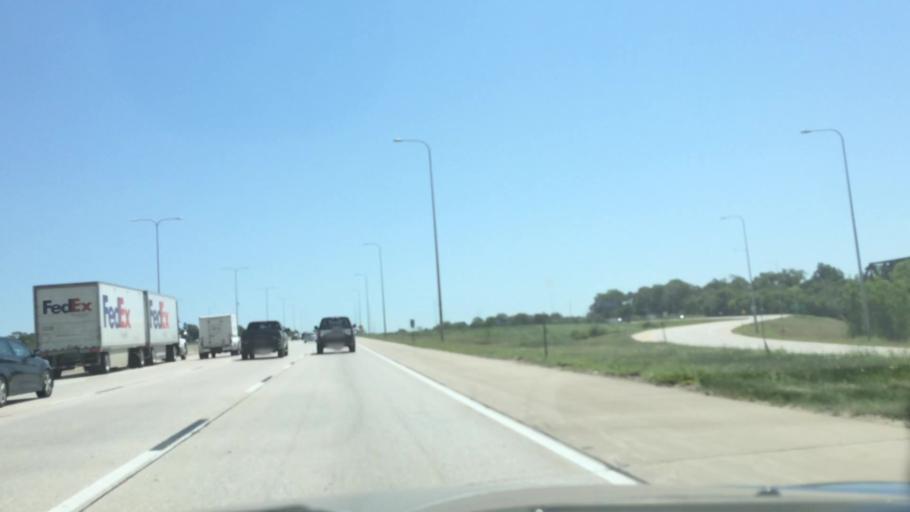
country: US
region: Nebraska
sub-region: Douglas County
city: Ralston
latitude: 41.2236
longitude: -96.0098
